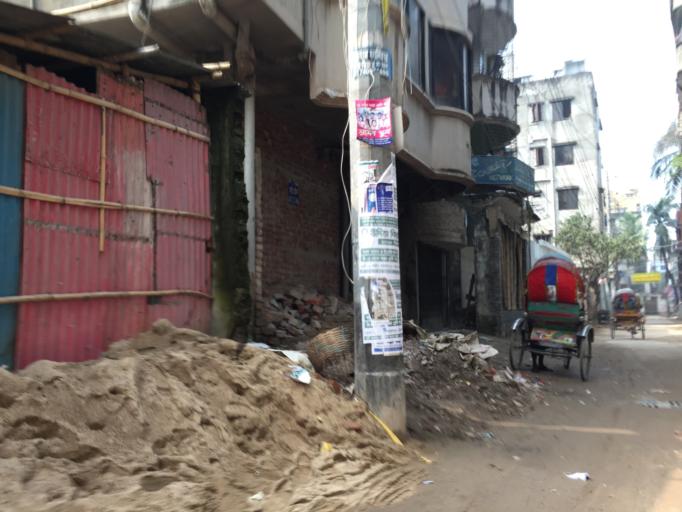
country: BD
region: Dhaka
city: Azimpur
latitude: 23.7879
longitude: 90.3618
